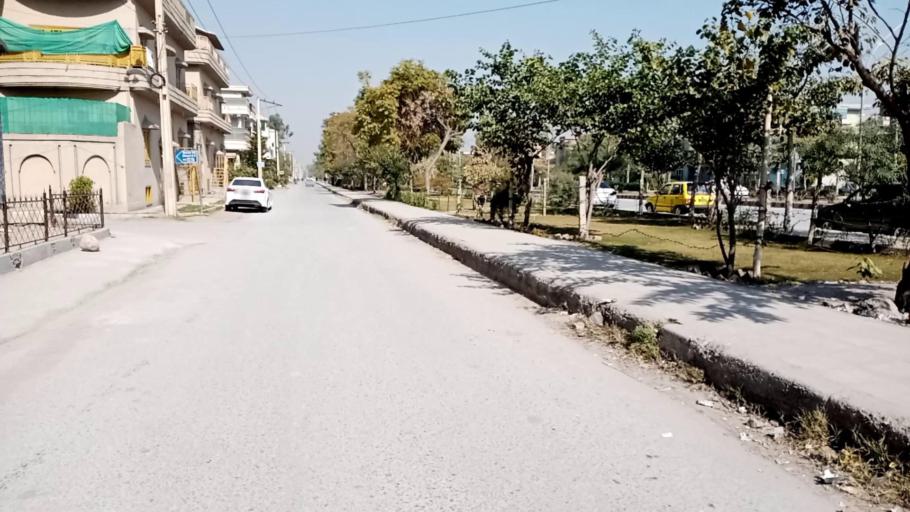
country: PK
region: Khyber Pakhtunkhwa
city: Peshawar
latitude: 33.9527
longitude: 71.4326
